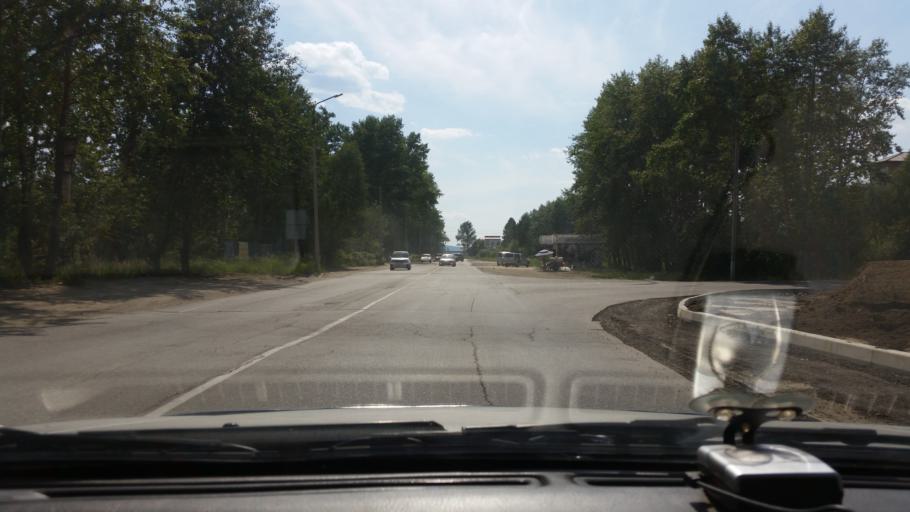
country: RU
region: Irkutsk
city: Shelekhov
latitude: 52.2043
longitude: 104.0829
